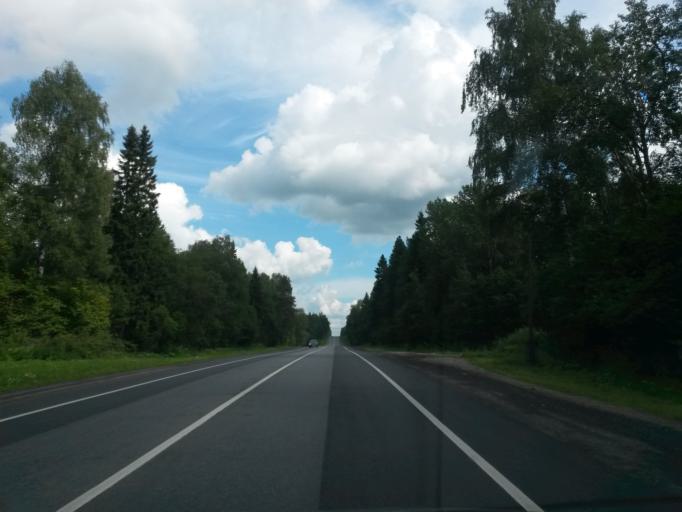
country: RU
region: Jaroslavl
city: Pereslavl'-Zalesskiy
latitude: 56.6705
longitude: 38.7220
